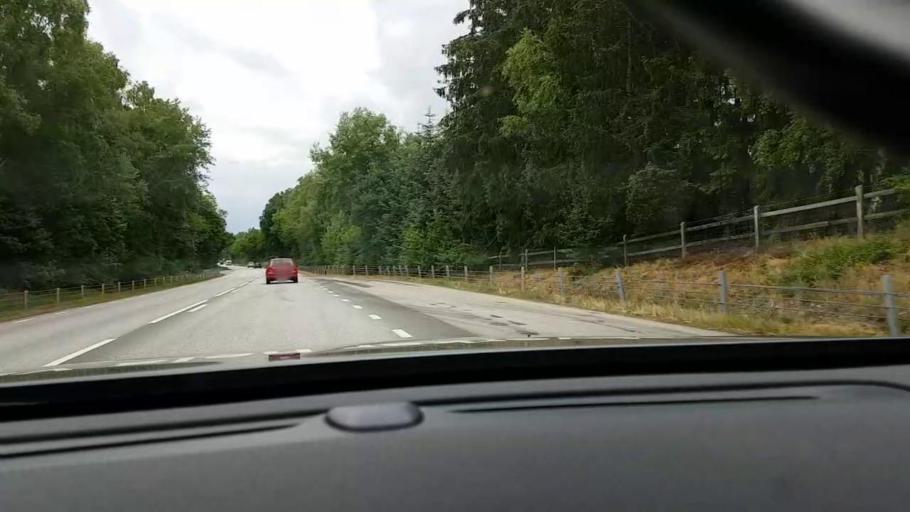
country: SE
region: Skane
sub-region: Hoors Kommun
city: Satofta
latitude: 55.9068
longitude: 13.6071
